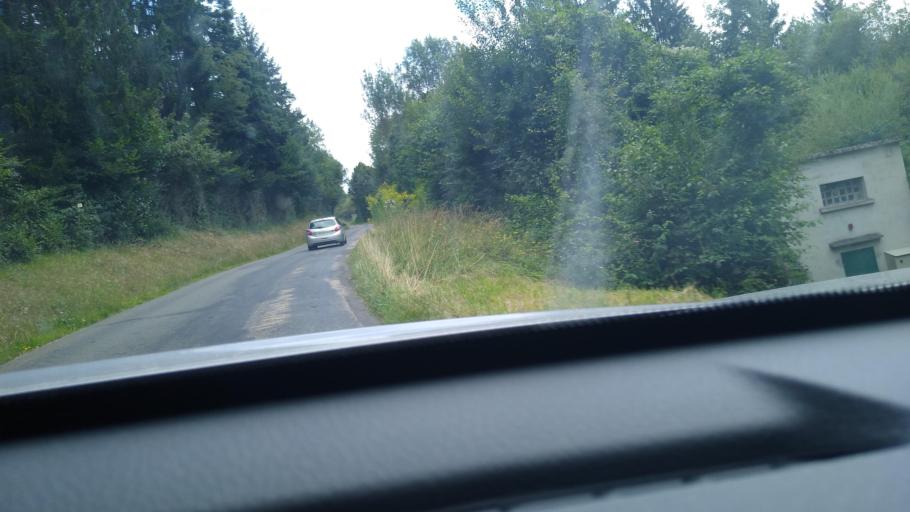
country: FR
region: Rhone-Alpes
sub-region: Departement de l'Ain
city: Saint-Martin-du-Frene
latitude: 46.1318
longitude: 5.5595
